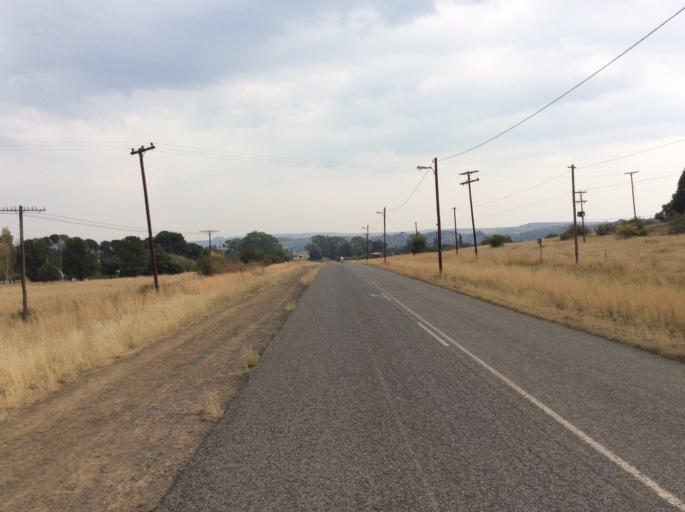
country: LS
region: Mafeteng
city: Mafeteng
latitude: -29.9870
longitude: 27.0214
